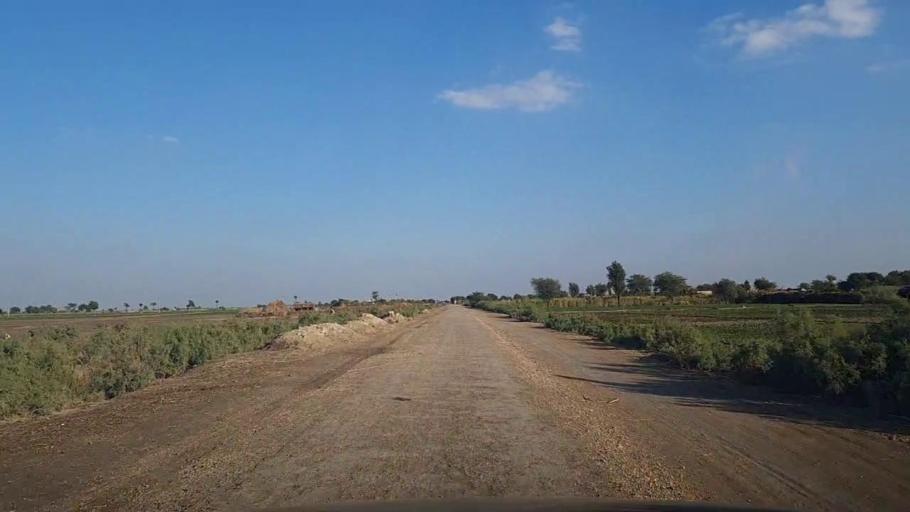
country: PK
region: Sindh
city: Jhol
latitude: 25.9228
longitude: 69.0279
